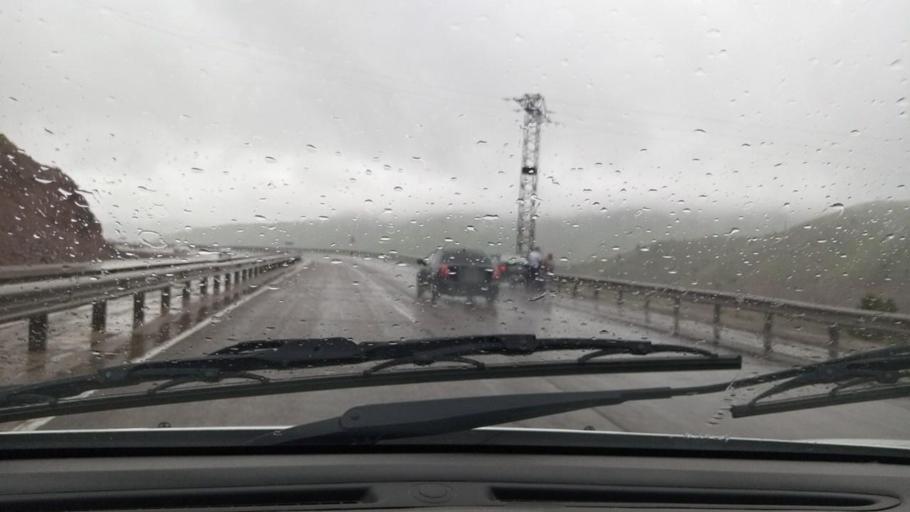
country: UZ
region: Toshkent
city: Angren
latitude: 41.0889
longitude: 70.5354
